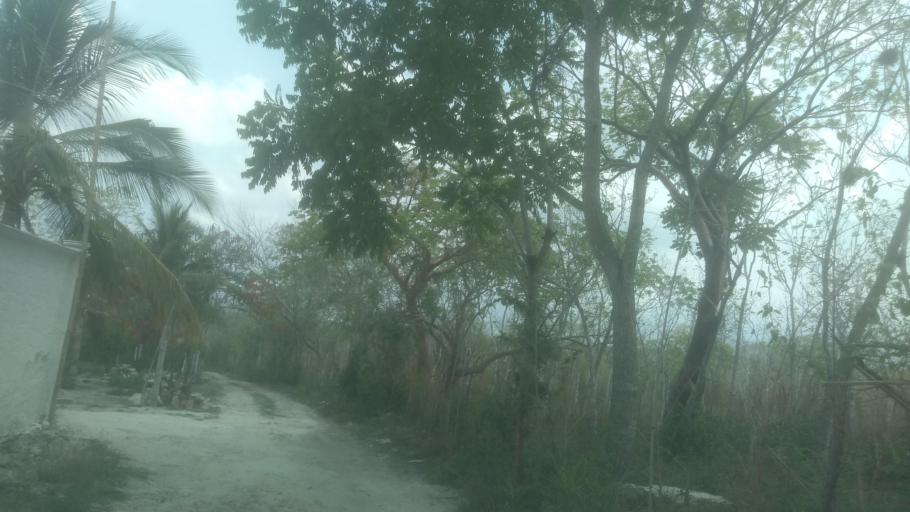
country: MX
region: Veracruz
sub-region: Emiliano Zapata
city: Plan del Rio
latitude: 19.3879
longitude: -96.6356
